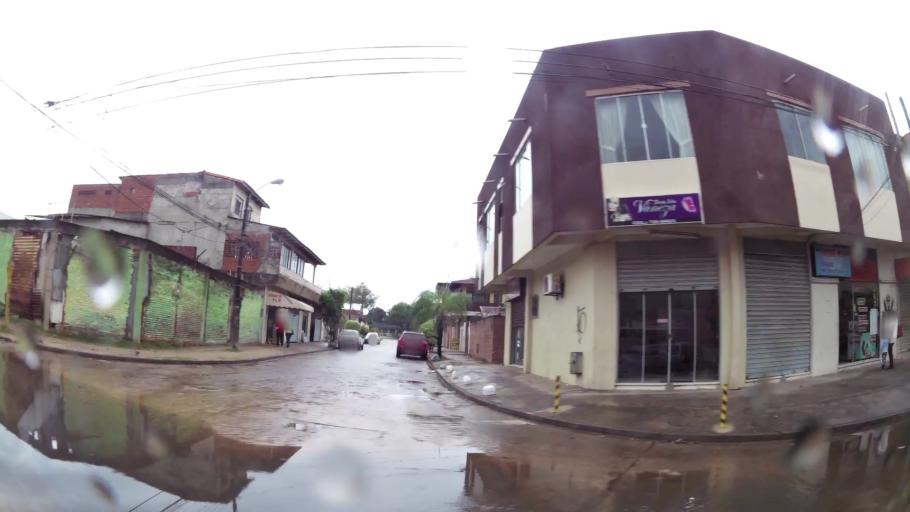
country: BO
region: Santa Cruz
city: Santa Cruz de la Sierra
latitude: -17.8026
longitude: -63.1915
